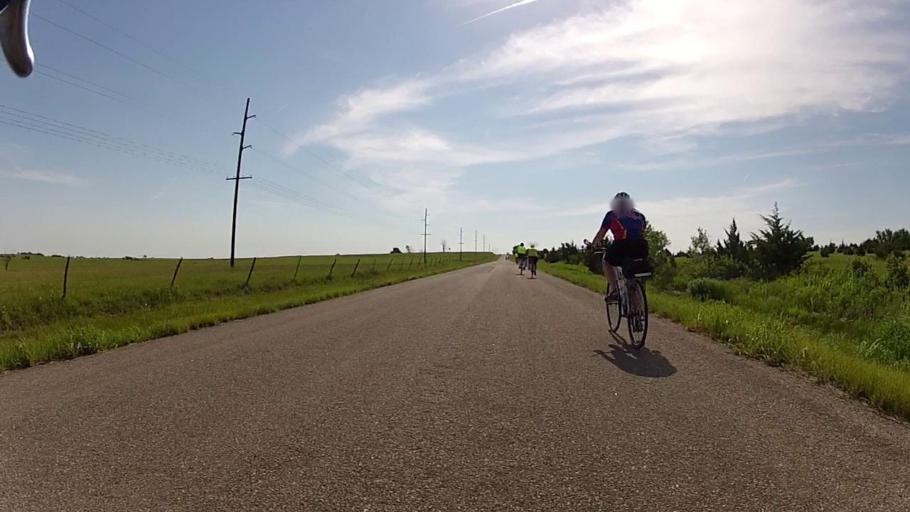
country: US
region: Kansas
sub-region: Cowley County
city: Winfield
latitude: 37.0710
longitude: -96.6519
